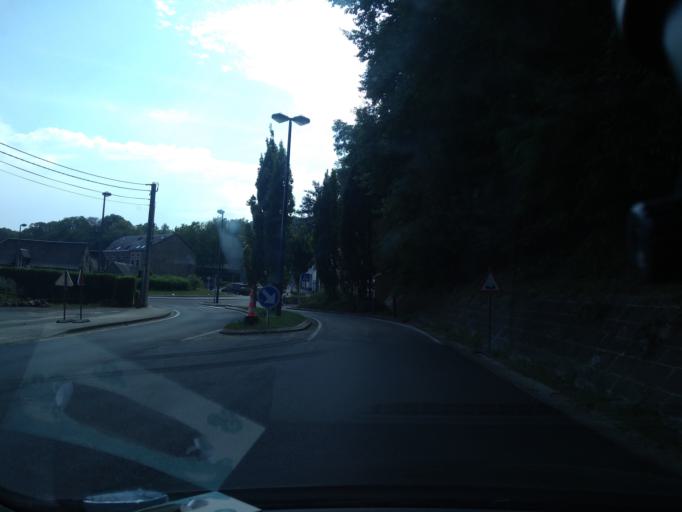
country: BE
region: Wallonia
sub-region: Province de Namur
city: Profondeville
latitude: 50.3494
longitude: 4.8515
